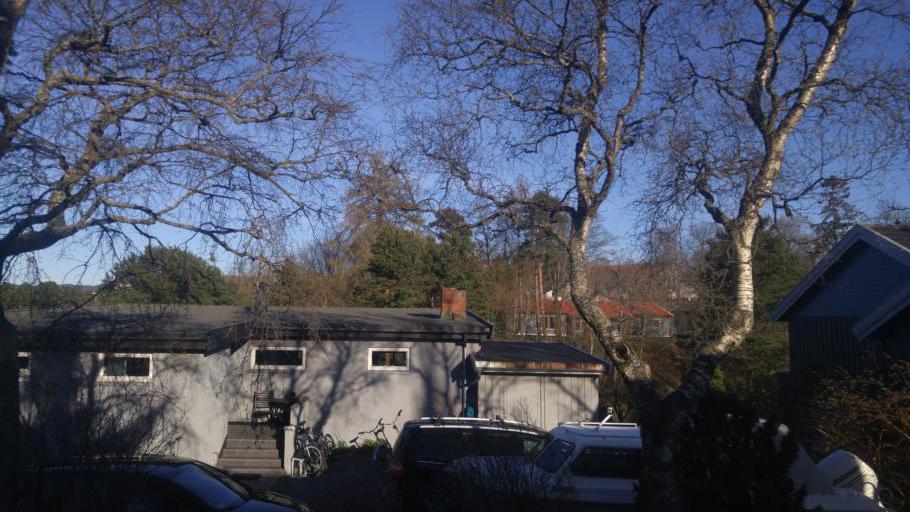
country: NO
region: Sor-Trondelag
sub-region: Trondheim
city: Trondheim
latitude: 63.4263
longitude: 10.4595
